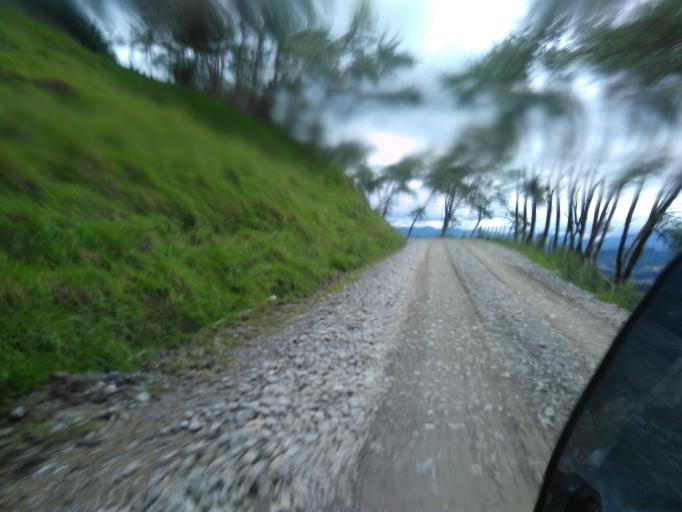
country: NZ
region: Gisborne
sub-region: Gisborne District
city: Gisborne
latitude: -38.0909
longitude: 178.0834
